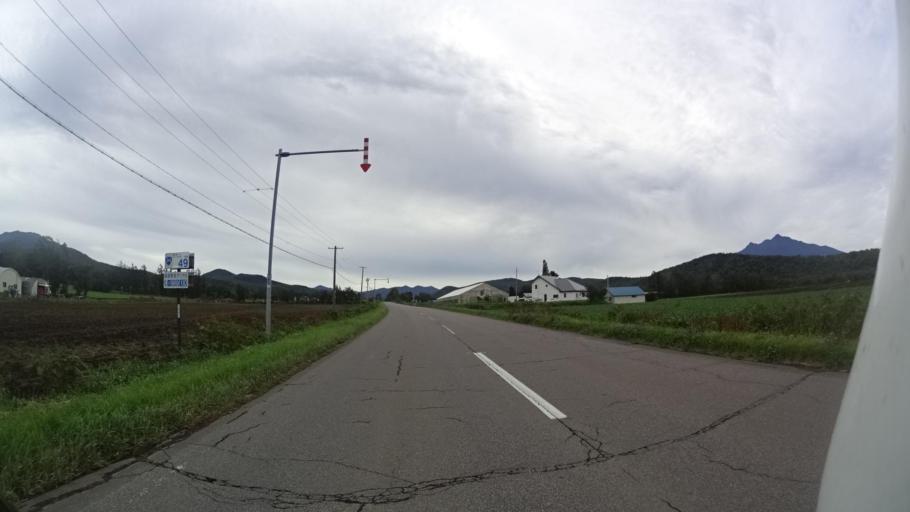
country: JP
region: Hokkaido
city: Shibetsu
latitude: 43.8675
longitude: 144.7517
